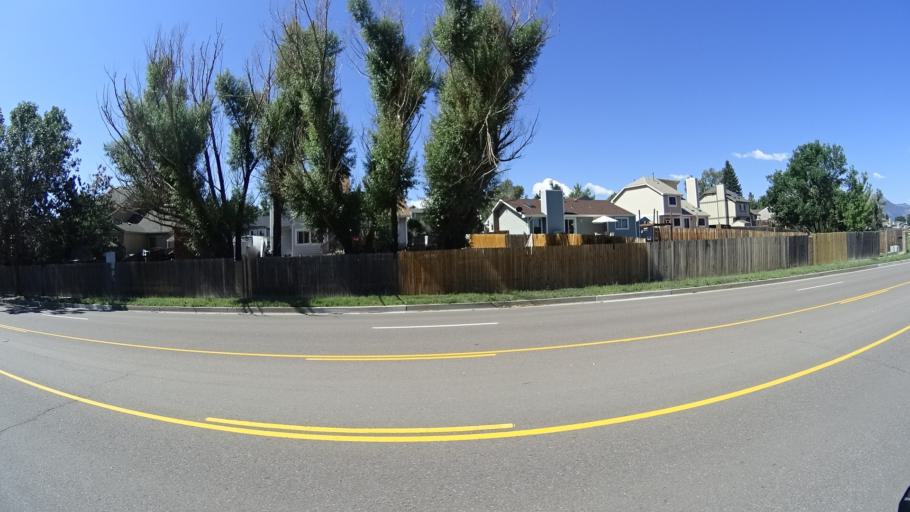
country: US
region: Colorado
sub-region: El Paso County
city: Black Forest
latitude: 38.9463
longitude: -104.7672
